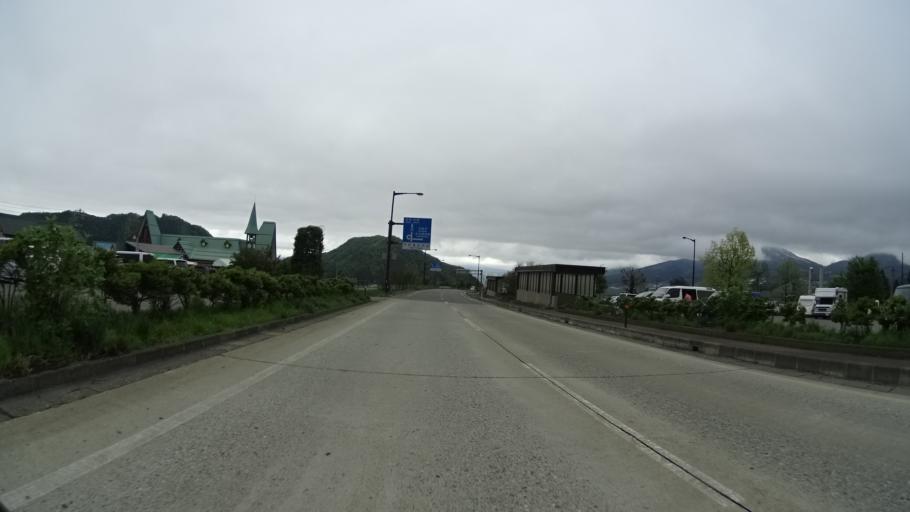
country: JP
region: Nagano
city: Nakano
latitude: 36.7411
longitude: 138.4056
